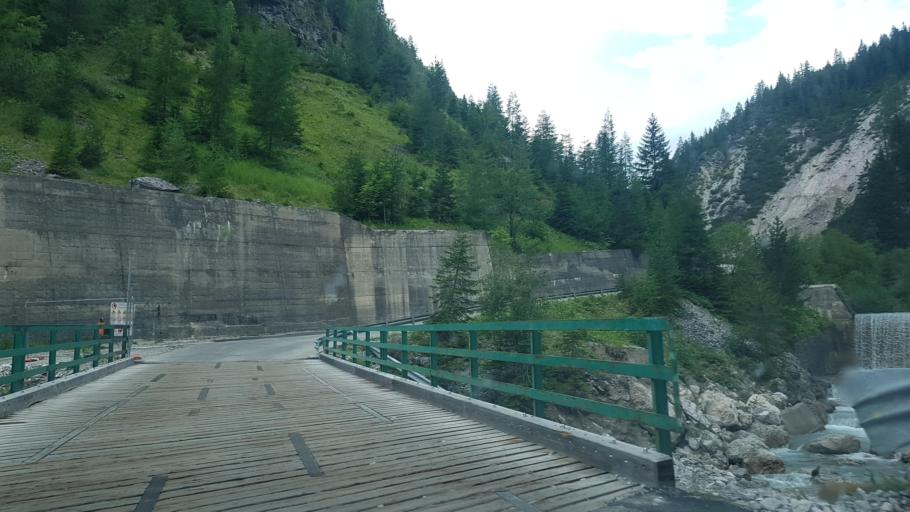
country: IT
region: Veneto
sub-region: Provincia di Belluno
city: San Pietro di Cadore
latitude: 46.5932
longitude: 12.6313
